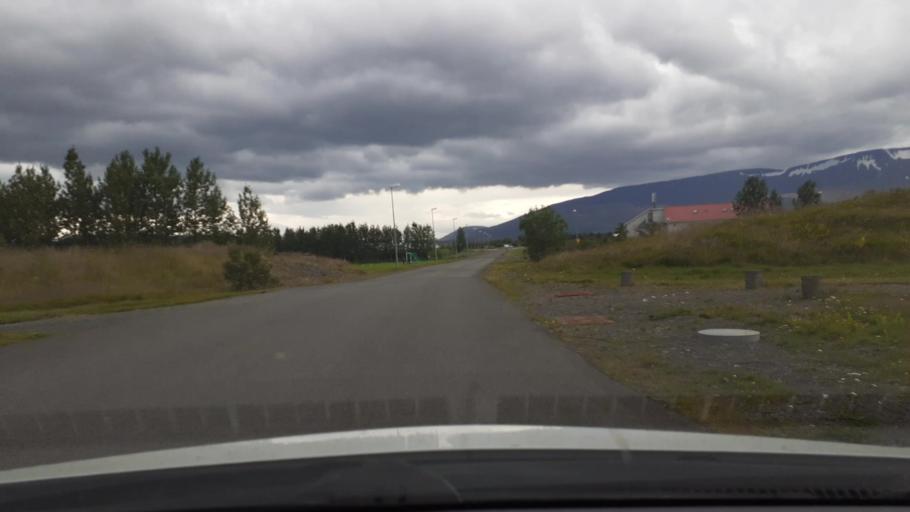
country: IS
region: West
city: Borgarnes
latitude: 64.5622
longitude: -21.7688
